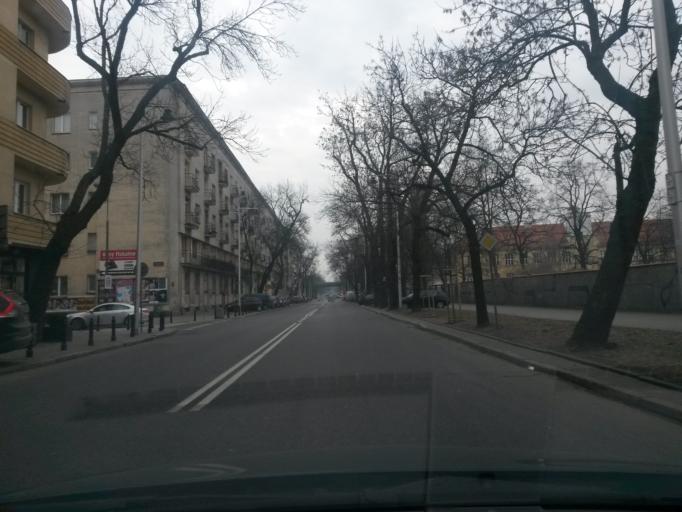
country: PL
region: Masovian Voivodeship
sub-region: Warszawa
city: Srodmiescie
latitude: 52.2244
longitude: 21.0348
